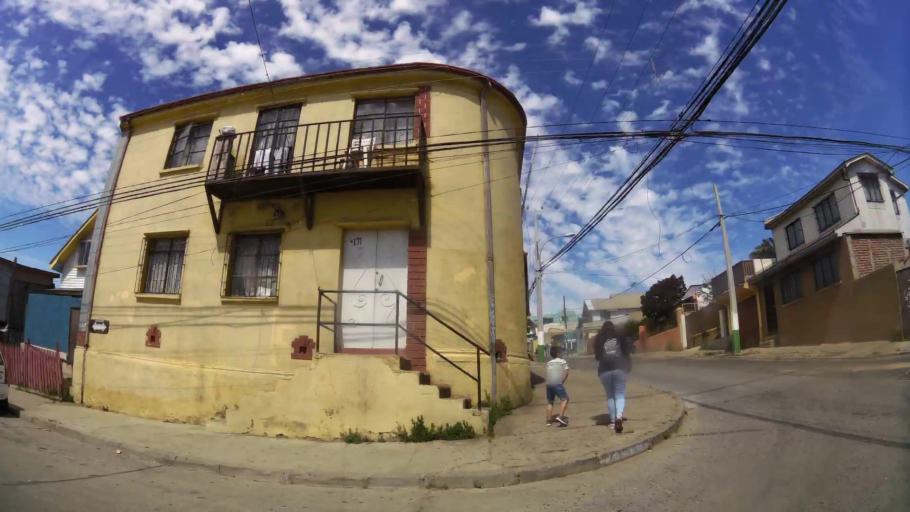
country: CL
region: Valparaiso
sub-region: Provincia de Valparaiso
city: Vina del Mar
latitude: -33.0375
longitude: -71.5828
